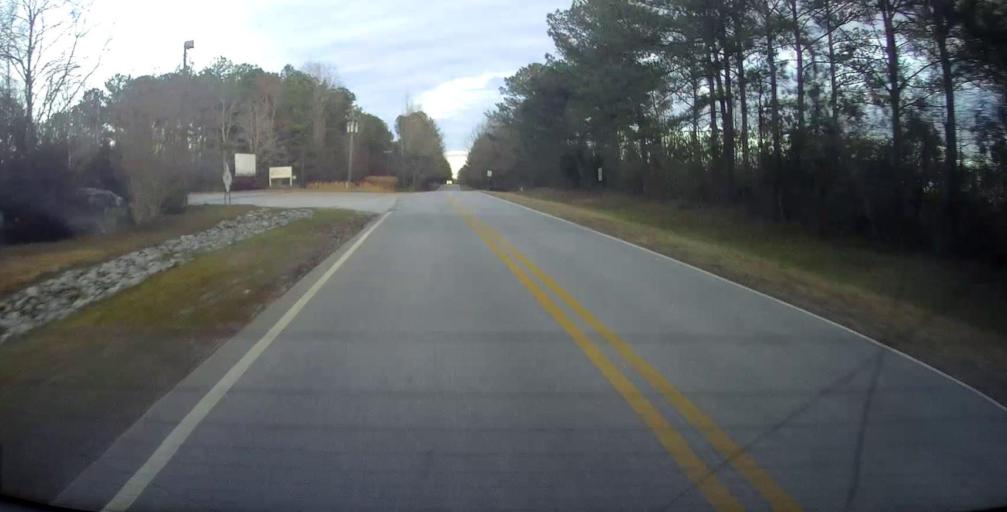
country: US
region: Alabama
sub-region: Russell County
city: Phenix City
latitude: 32.5969
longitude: -84.9055
